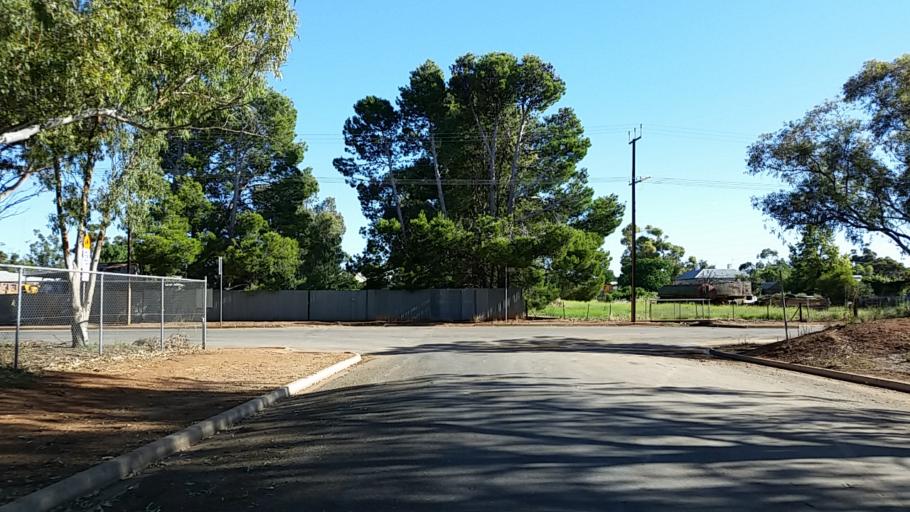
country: AU
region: South Australia
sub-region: Peterborough
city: Peterborough
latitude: -32.9725
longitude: 138.8317
